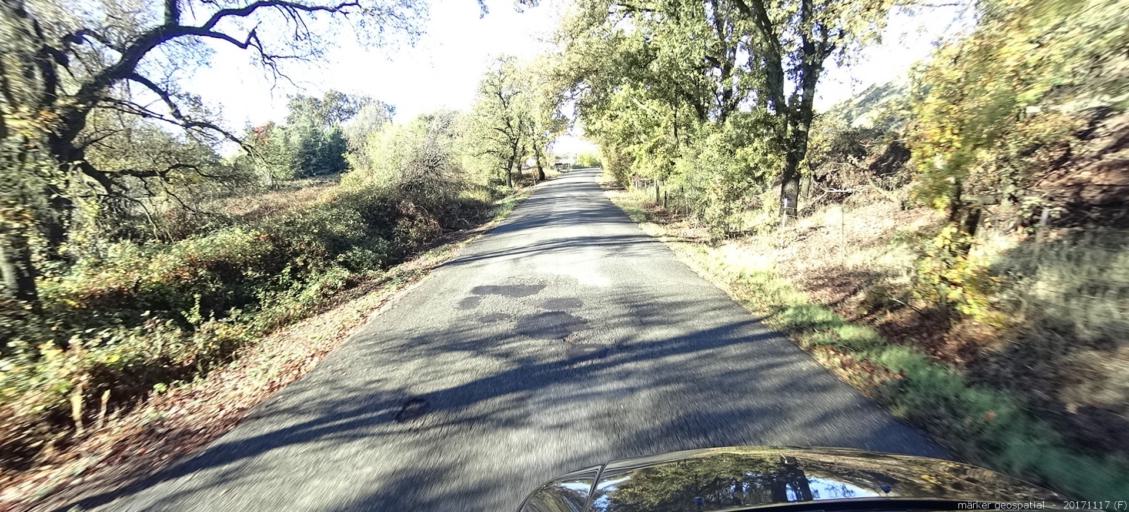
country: US
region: California
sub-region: Shasta County
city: Cottonwood
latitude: 40.3988
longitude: -122.1779
